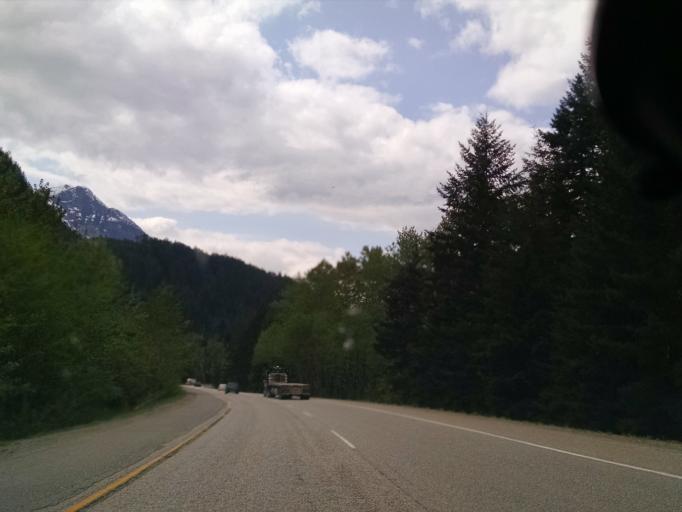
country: CA
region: British Columbia
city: Hope
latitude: 49.3790
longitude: -121.3399
